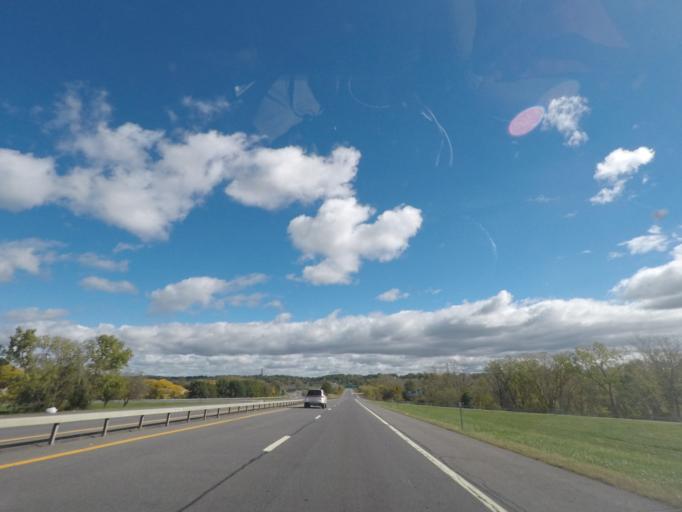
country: US
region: New York
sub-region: Albany County
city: Menands
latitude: 42.6983
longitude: -73.7180
